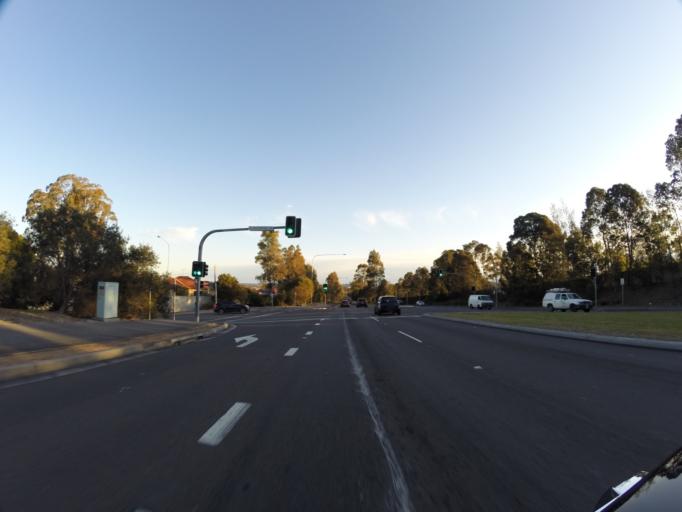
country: AU
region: New South Wales
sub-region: Fairfield
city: Cecil Park
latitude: -33.8890
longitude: 150.8610
